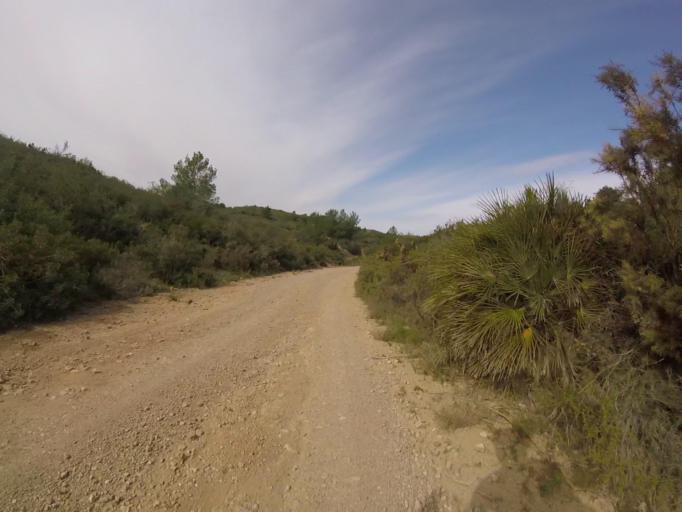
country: ES
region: Valencia
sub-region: Provincia de Castello
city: Torreblanca
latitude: 40.2040
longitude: 0.1417
